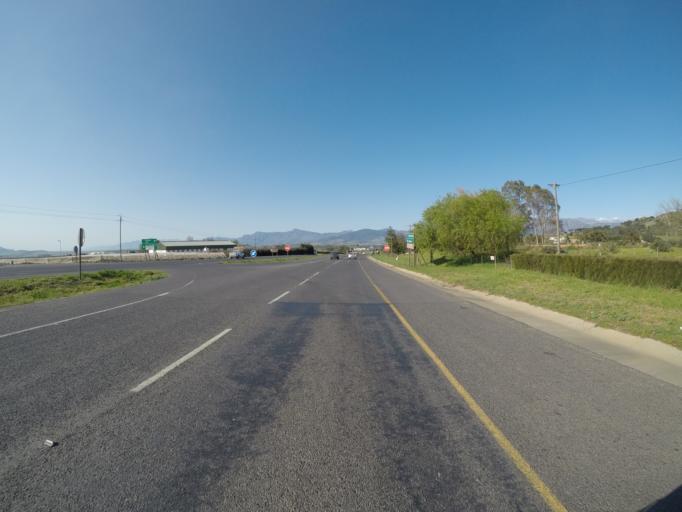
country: ZA
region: Western Cape
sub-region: Cape Winelands District Municipality
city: Noorder-Paarl
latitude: -33.6717
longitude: 18.9105
